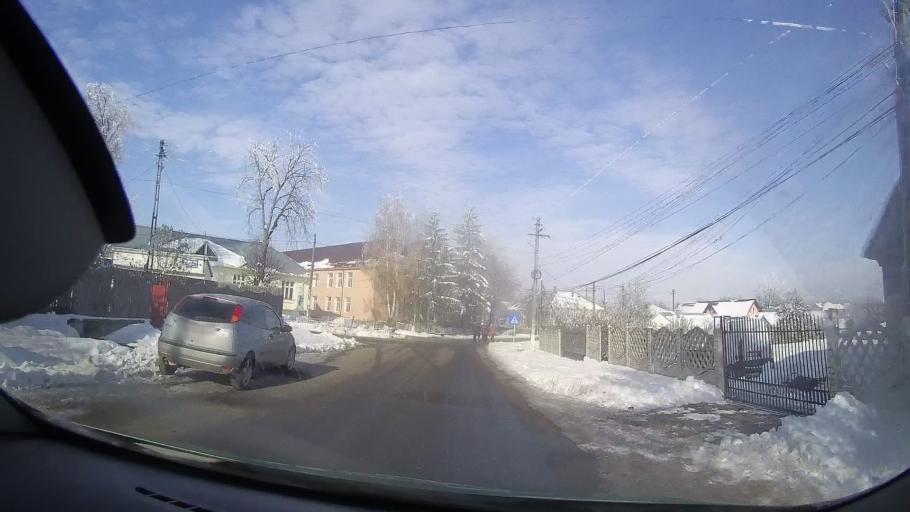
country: RO
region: Iasi
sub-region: Comuna Cristesti
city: Cristesti
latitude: 47.2595
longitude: 26.5748
